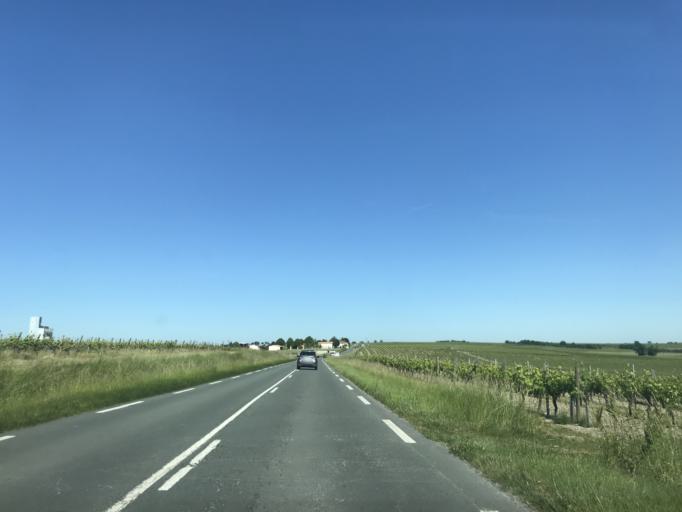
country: FR
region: Poitou-Charentes
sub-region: Departement de la Charente-Maritime
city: Perignac
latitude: 45.5629
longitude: -0.3910
